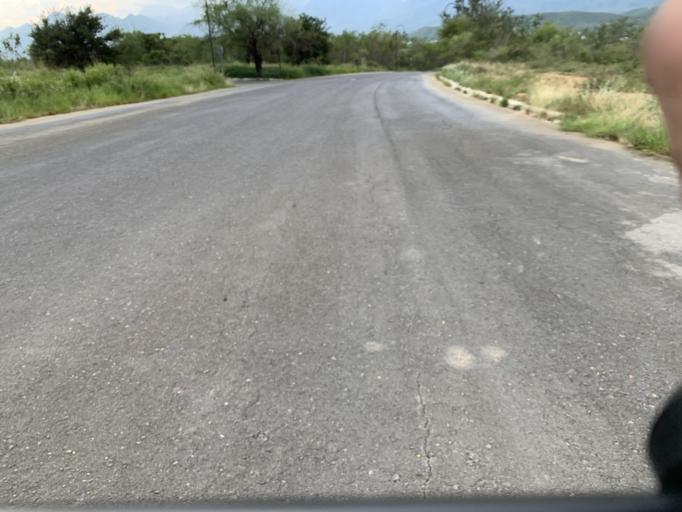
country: MX
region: Nuevo Leon
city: Santiago
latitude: 25.5060
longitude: -100.1808
